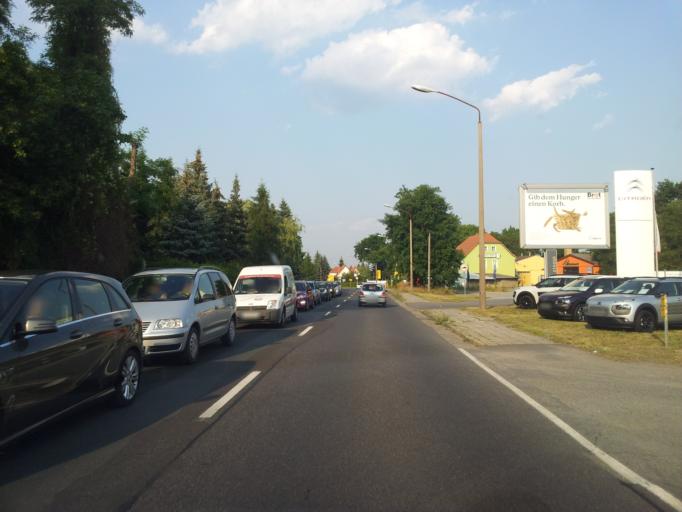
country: DE
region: Saxony
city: Hoyerswerda
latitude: 51.4243
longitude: 14.2182
